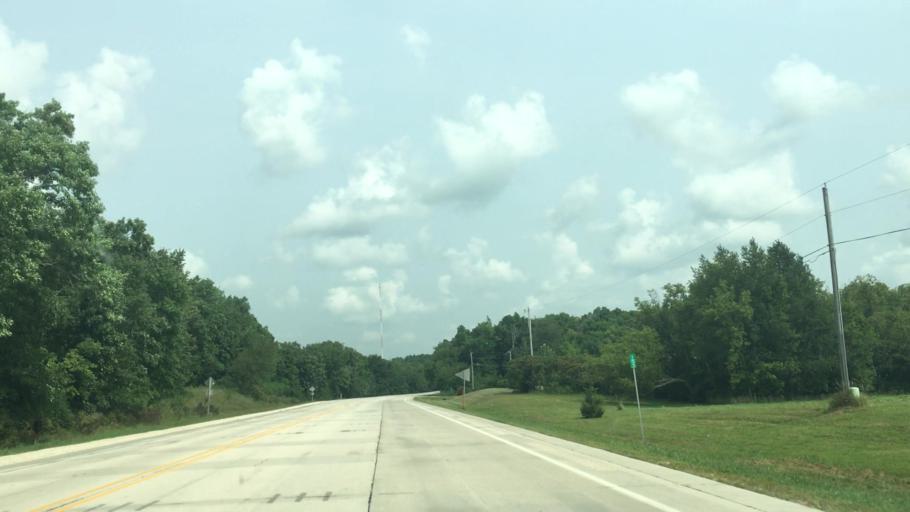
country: US
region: Iowa
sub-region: Winneshiek County
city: Decorah
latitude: 43.3369
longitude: -91.8121
